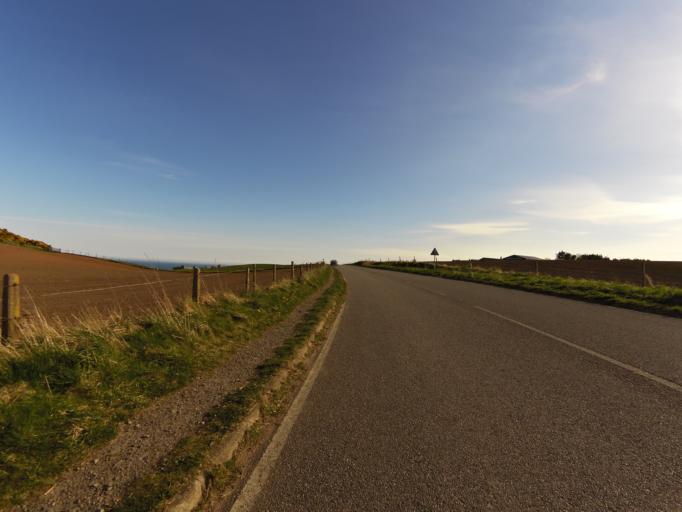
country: GB
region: Scotland
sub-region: Aberdeenshire
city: Stonehaven
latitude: 56.9551
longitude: -2.2057
